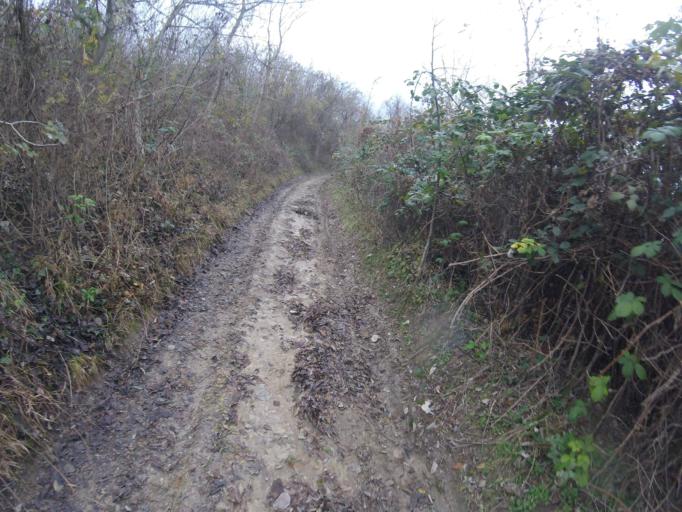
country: HU
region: Tolna
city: Szekszard
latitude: 46.3234
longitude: 18.6588
